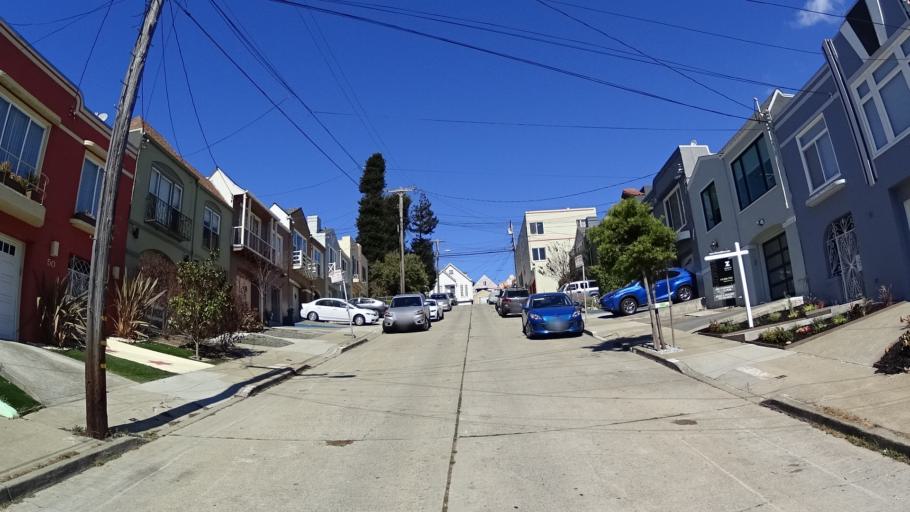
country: US
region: California
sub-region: San Francisco County
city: San Francisco
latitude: 37.7343
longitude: -122.4197
